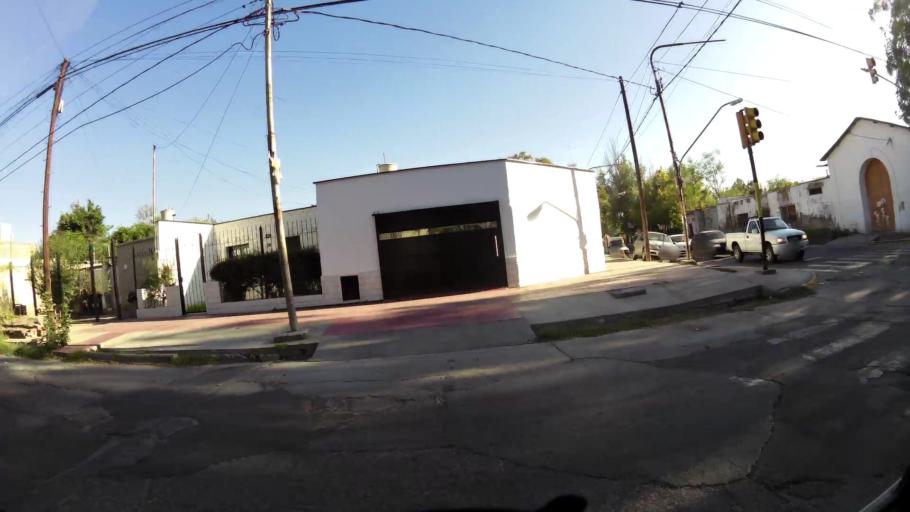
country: AR
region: Mendoza
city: Las Heras
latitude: -32.8596
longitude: -68.8277
